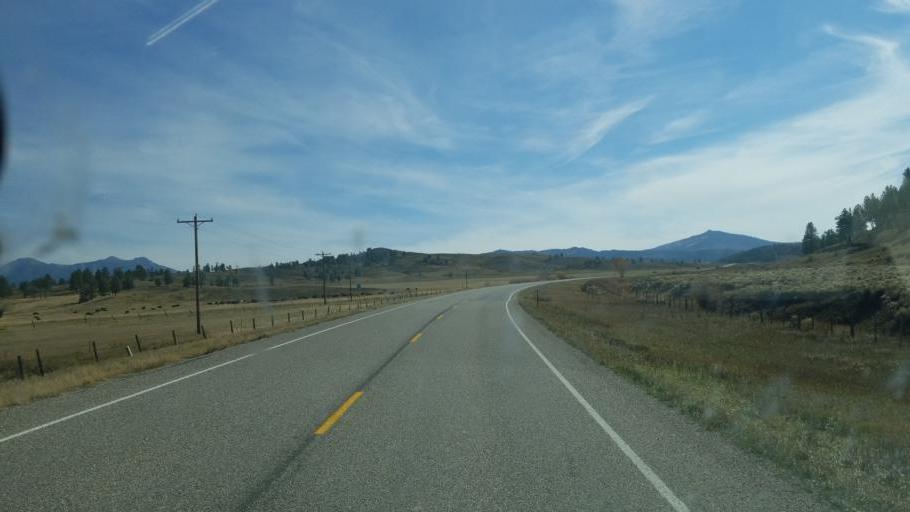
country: US
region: New Mexico
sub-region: Rio Arriba County
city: Dulce
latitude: 37.0335
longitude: -106.8329
